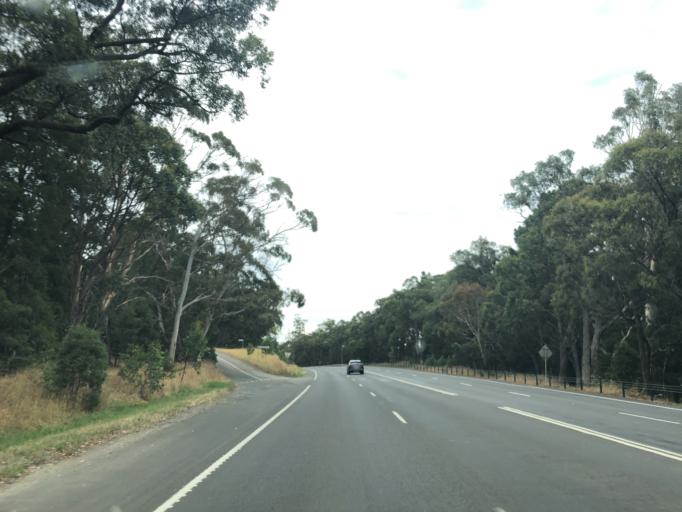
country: AU
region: Victoria
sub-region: Hume
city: Sunbury
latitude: -37.3838
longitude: 144.5267
